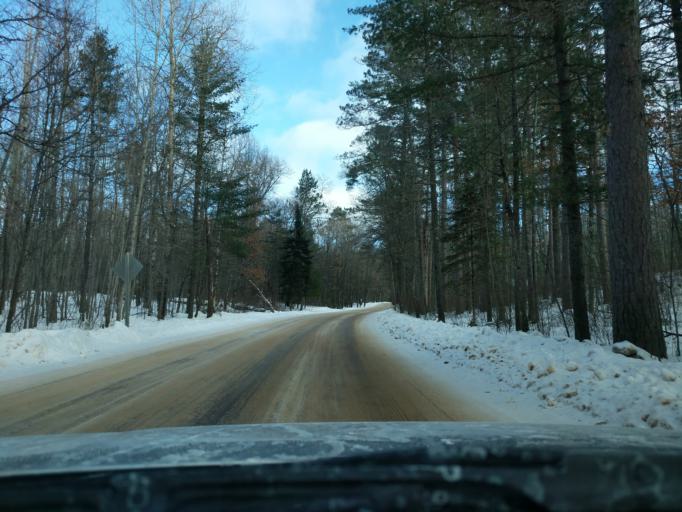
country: US
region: Wisconsin
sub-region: Vilas County
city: Eagle River
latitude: 45.7936
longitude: -89.0823
